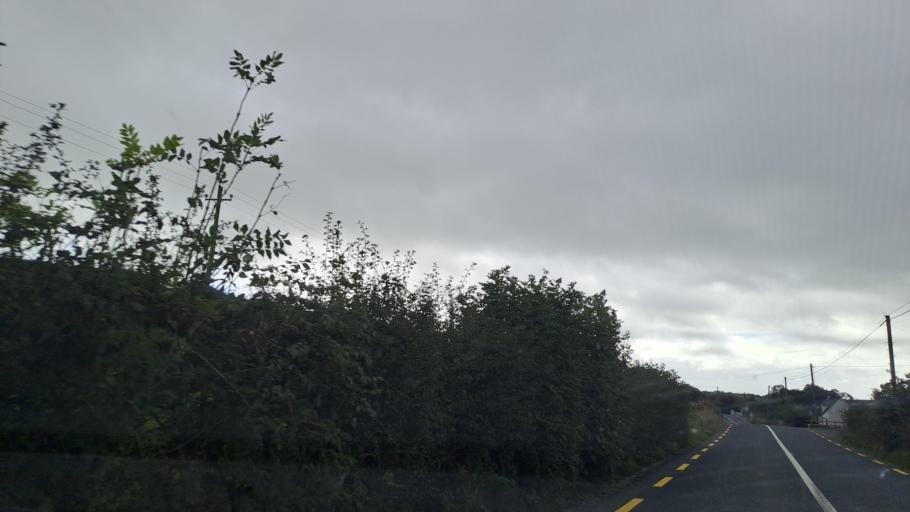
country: IE
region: Ulster
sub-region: An Cabhan
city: Bailieborough
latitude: 53.9527
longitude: -6.9513
